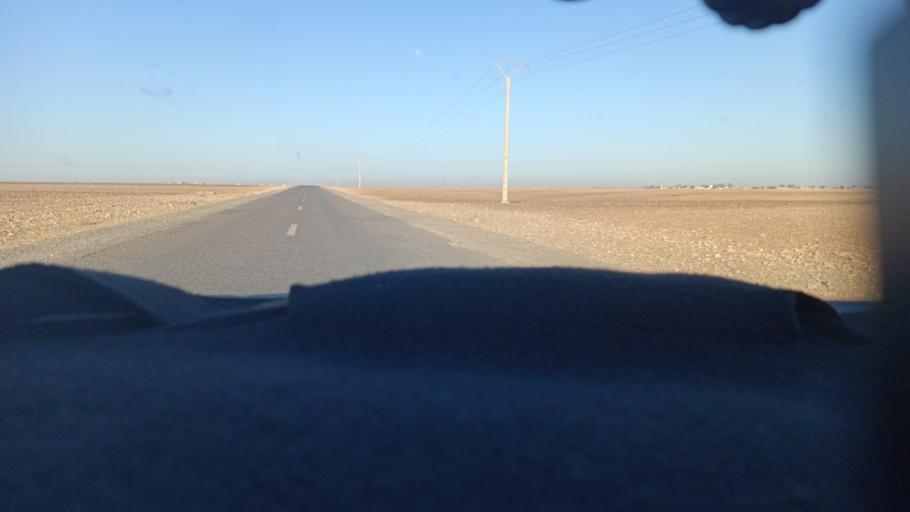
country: MA
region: Doukkala-Abda
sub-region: Safi
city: Youssoufia
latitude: 32.3719
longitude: -8.6384
